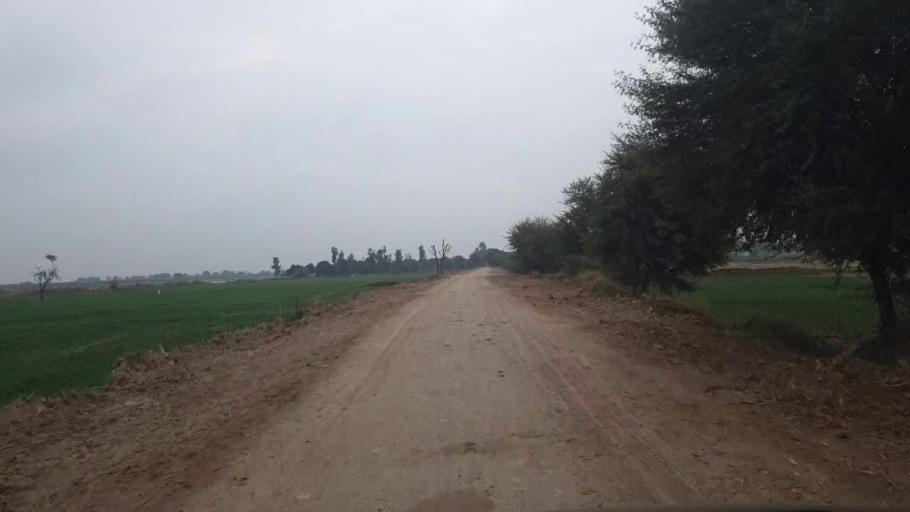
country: PK
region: Sindh
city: Shahdadpur
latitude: 25.8641
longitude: 68.6969
